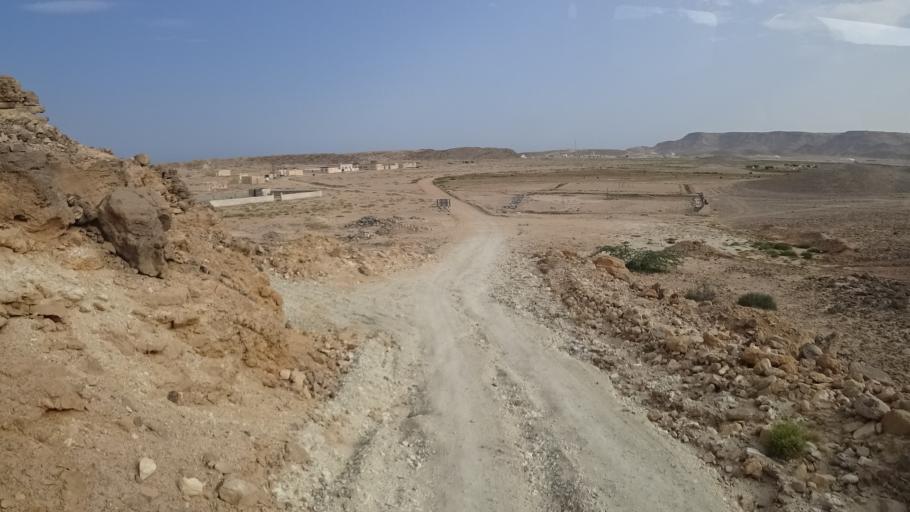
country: OM
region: Ash Sharqiyah
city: Sur
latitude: 22.4515
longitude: 59.8251
